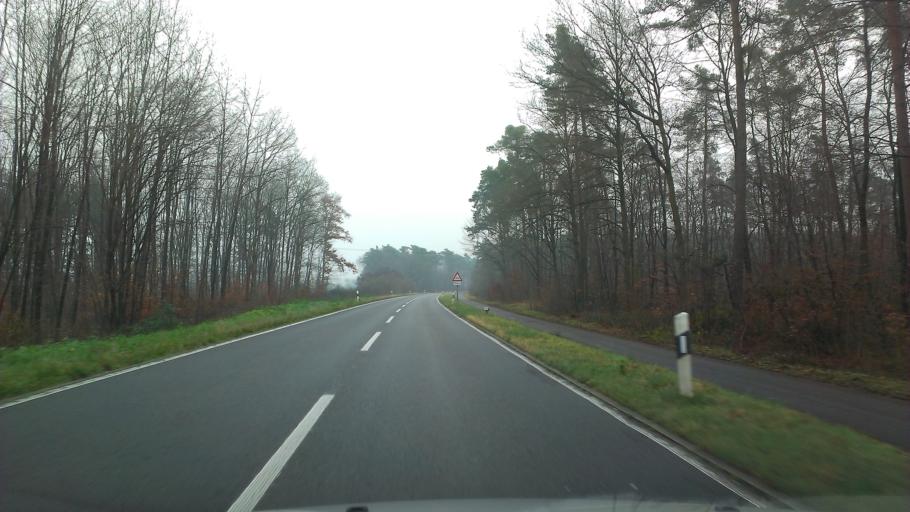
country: DE
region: Baden-Wuerttemberg
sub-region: Karlsruhe Region
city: Forst
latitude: 49.1747
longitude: 8.5955
